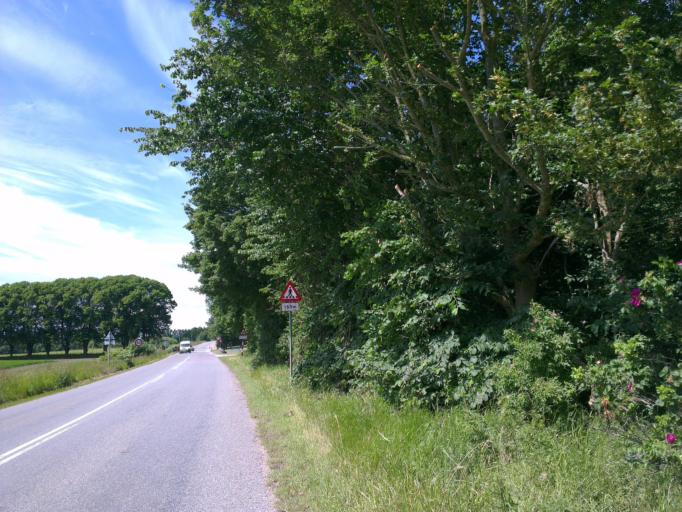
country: DK
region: Capital Region
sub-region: Frederikssund Kommune
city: Skibby
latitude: 55.7893
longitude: 11.9495
